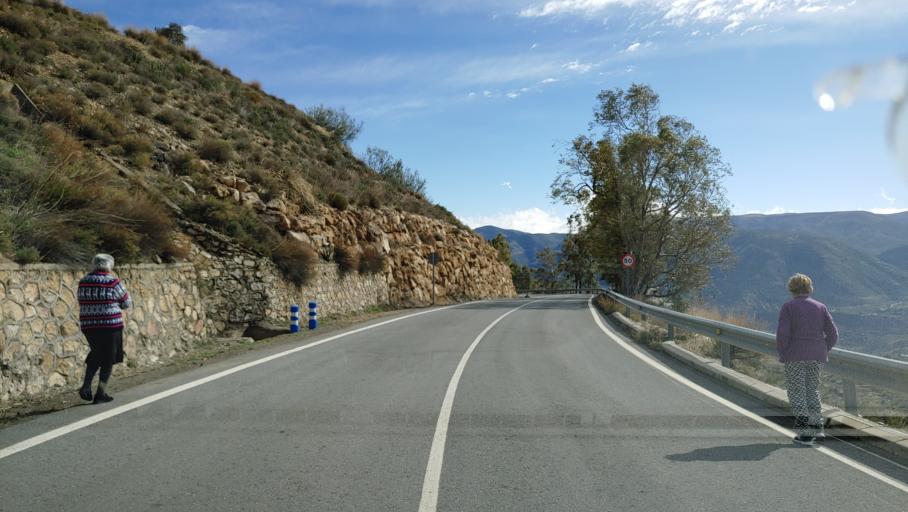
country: ES
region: Andalusia
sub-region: Provincia de Almeria
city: Ohanes
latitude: 37.0338
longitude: -2.7425
